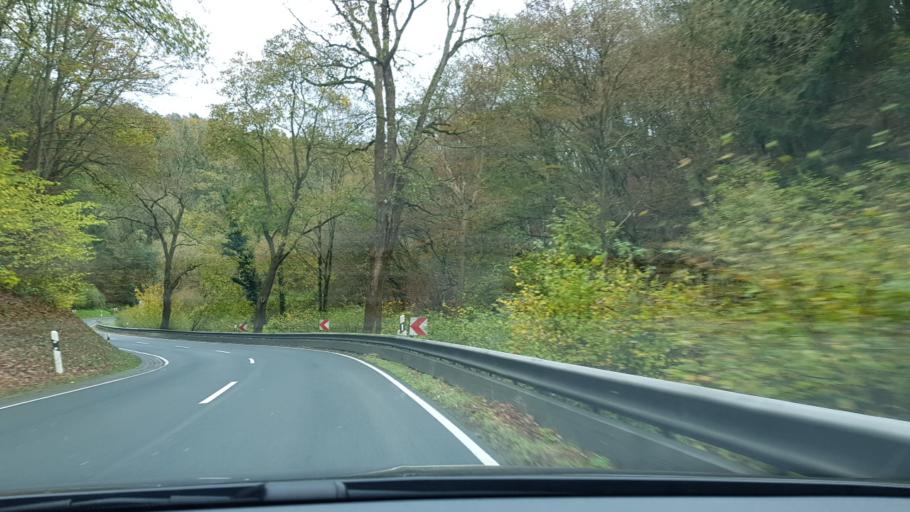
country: DE
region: Rheinland-Pfalz
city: Kalenborn
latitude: 50.5333
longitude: 6.9979
